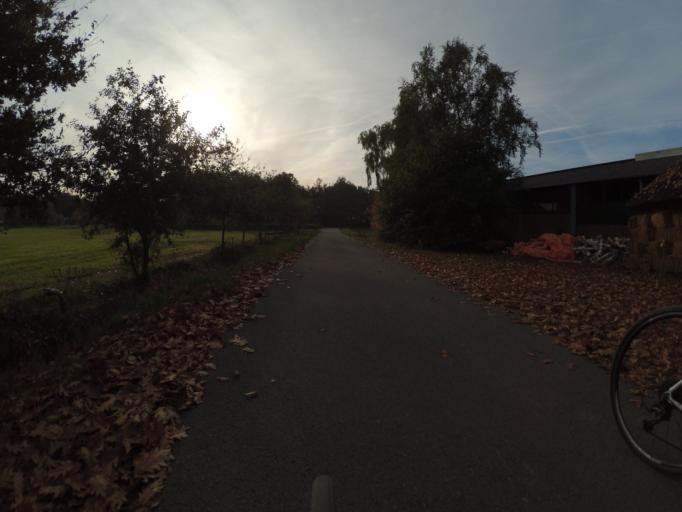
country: NL
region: Gelderland
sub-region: Gemeente Lochem
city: Harfsen
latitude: 52.2632
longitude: 6.3092
